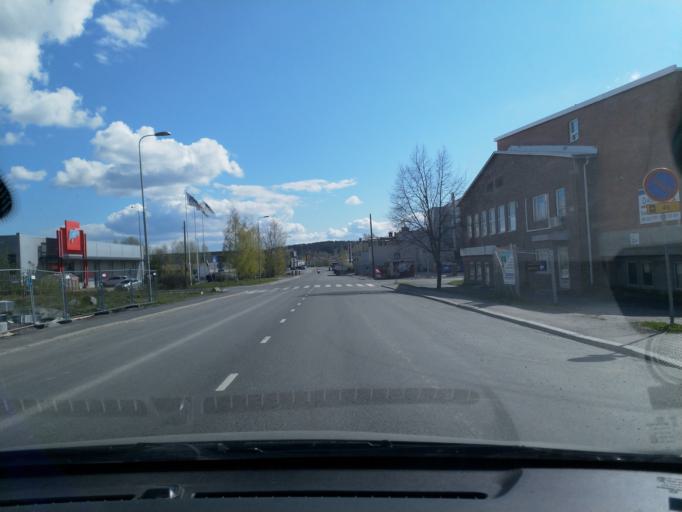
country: FI
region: Pirkanmaa
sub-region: Tampere
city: Tampere
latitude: 61.4816
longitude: 23.7894
